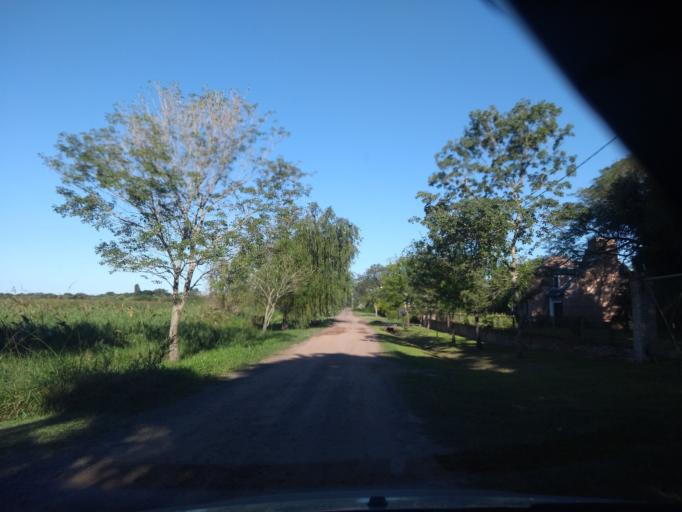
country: AR
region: Chaco
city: Barranqueras
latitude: -27.4384
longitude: -58.9084
